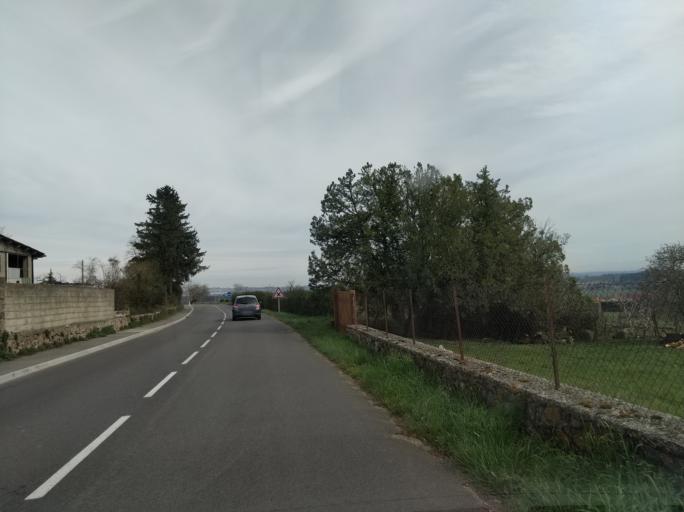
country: FR
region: Rhone-Alpes
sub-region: Departement de l'Ardeche
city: Roiffieux
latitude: 45.1953
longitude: 4.6497
